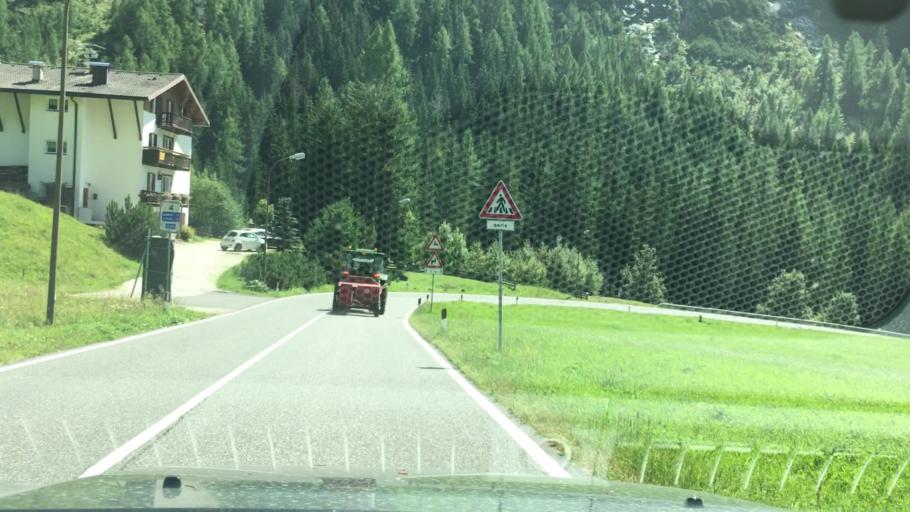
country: IT
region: Trentino-Alto Adige
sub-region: Provincia di Trento
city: Canazei
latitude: 46.4581
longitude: 11.8039
